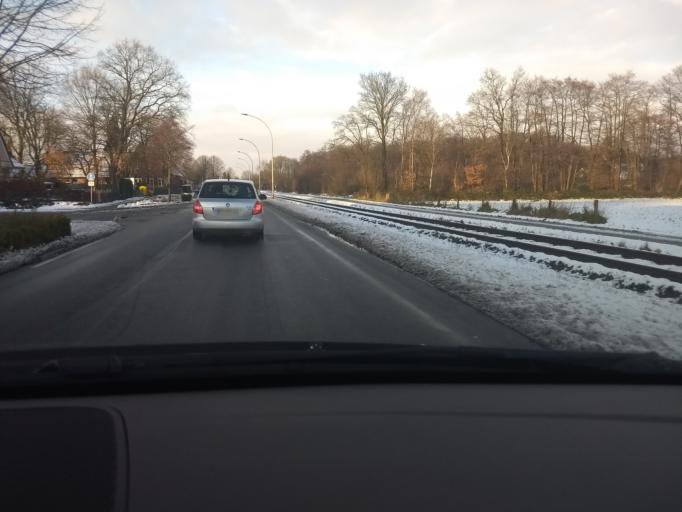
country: DE
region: Lower Saxony
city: Lage
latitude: 52.4891
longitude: 6.9833
